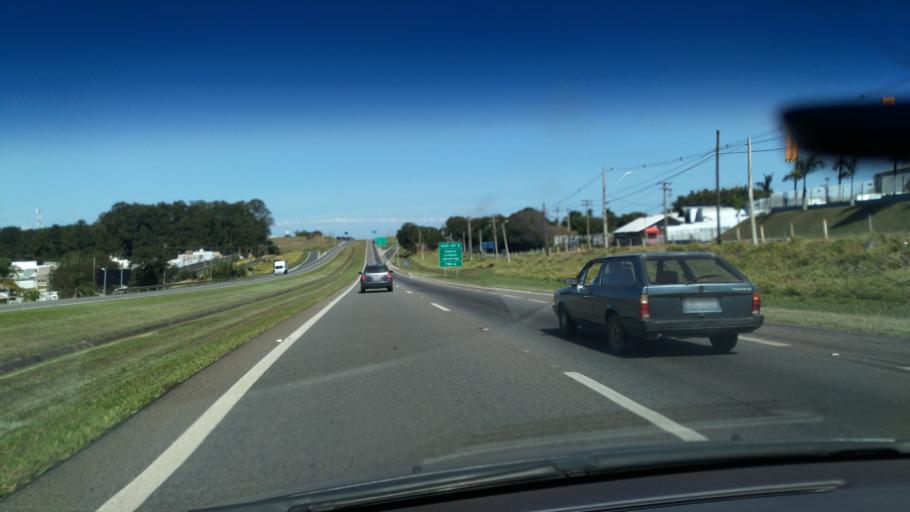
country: BR
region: Sao Paulo
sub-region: Mogi-Mirim
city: Mogi Mirim
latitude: -22.4682
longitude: -46.9820
